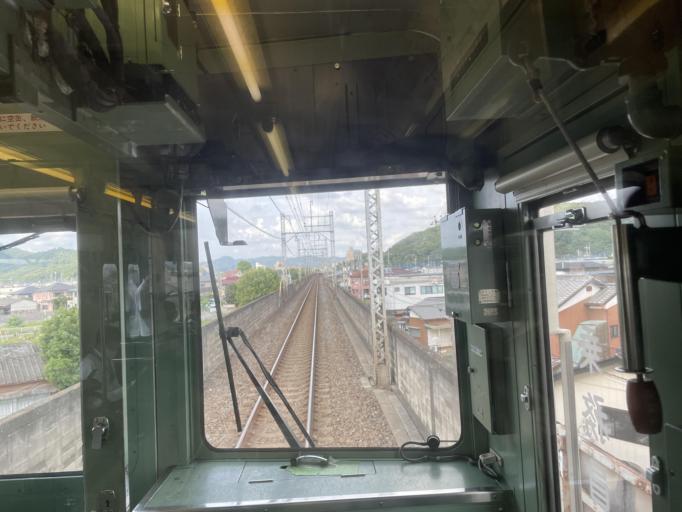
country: JP
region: Tochigi
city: Ashikaga
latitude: 36.3285
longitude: 139.4356
